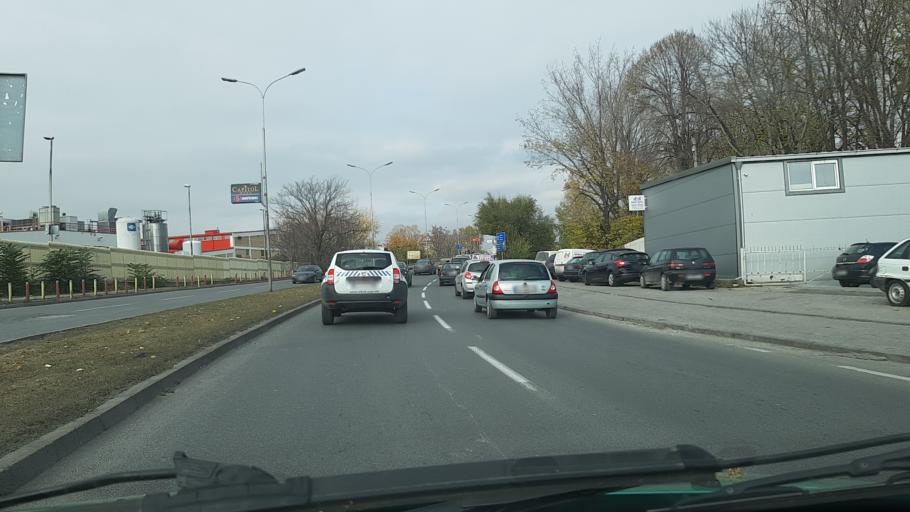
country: MK
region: Cair
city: Cair
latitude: 42.0006
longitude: 21.4715
